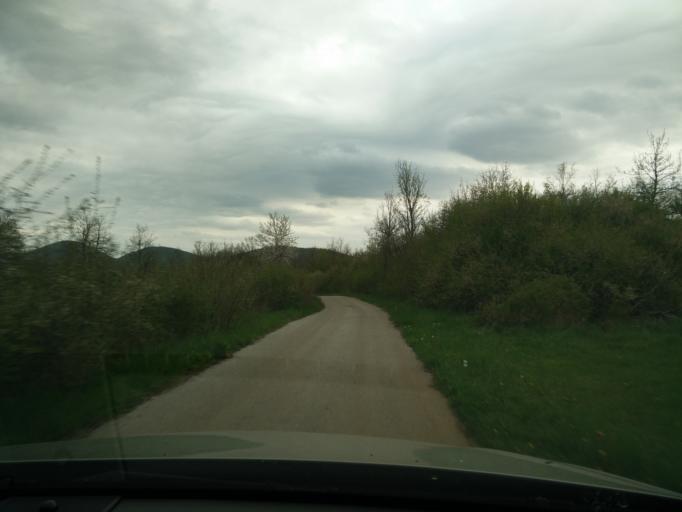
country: HR
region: Zadarska
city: Gracac
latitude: 44.3982
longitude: 15.6878
